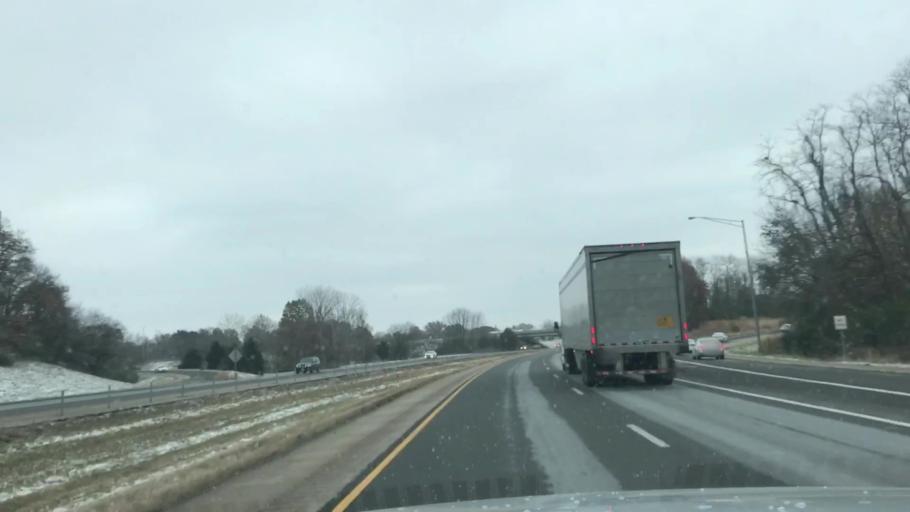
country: US
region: Illinois
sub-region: Madison County
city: Glen Carbon
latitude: 38.7567
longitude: -89.9606
